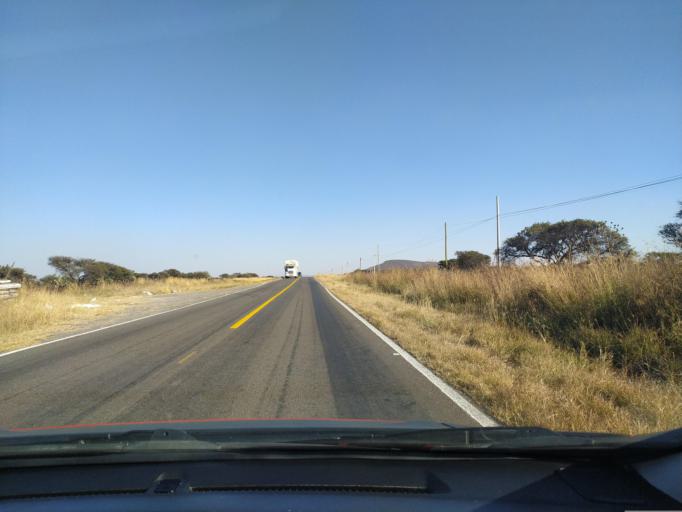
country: MX
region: Jalisco
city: San Miguel el Alto
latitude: 21.0175
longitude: -102.5000
